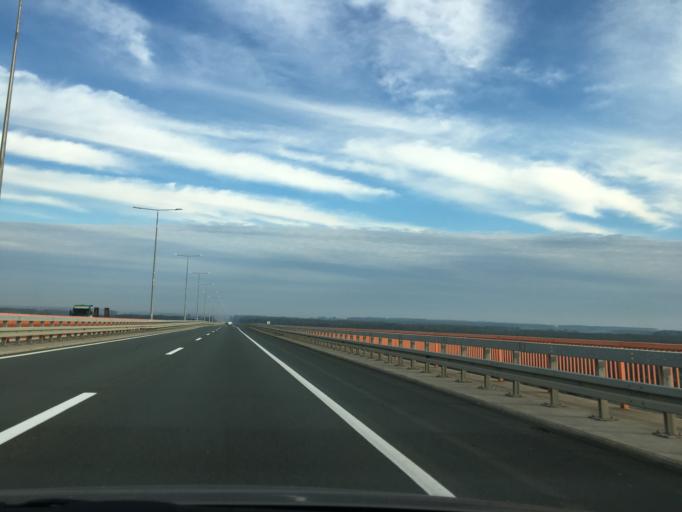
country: RS
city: Beska
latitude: 45.1676
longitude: 20.0803
